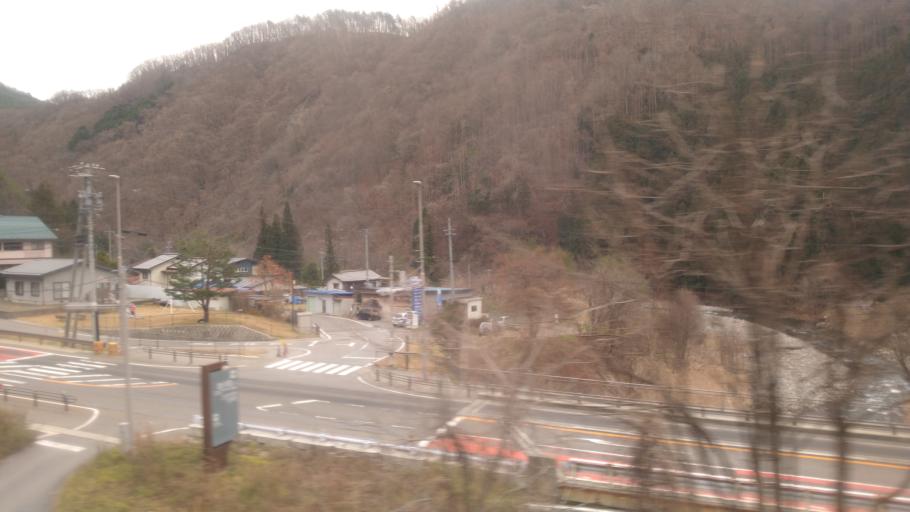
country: JP
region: Nagano
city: Tatsuno
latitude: 35.9983
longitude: 137.8512
